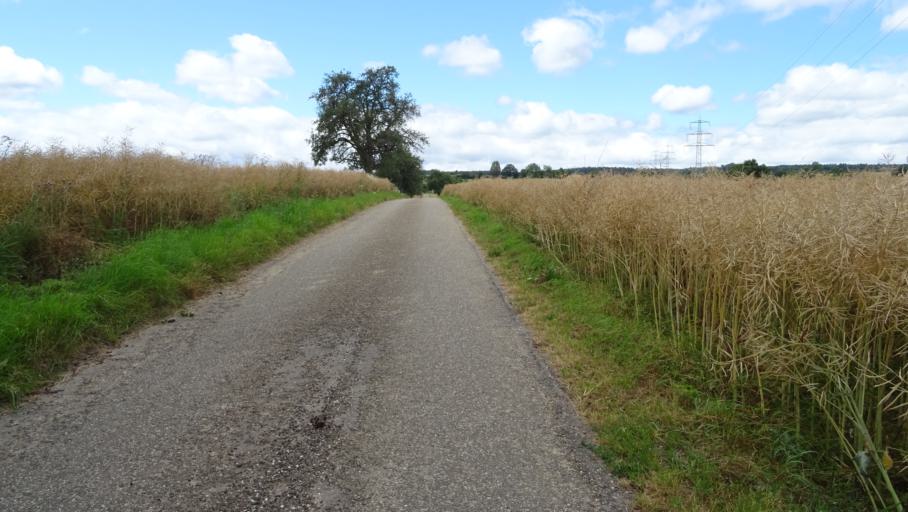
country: DE
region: Baden-Wuerttemberg
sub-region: Karlsruhe Region
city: Neunkirchen
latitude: 49.3835
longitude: 9.0216
